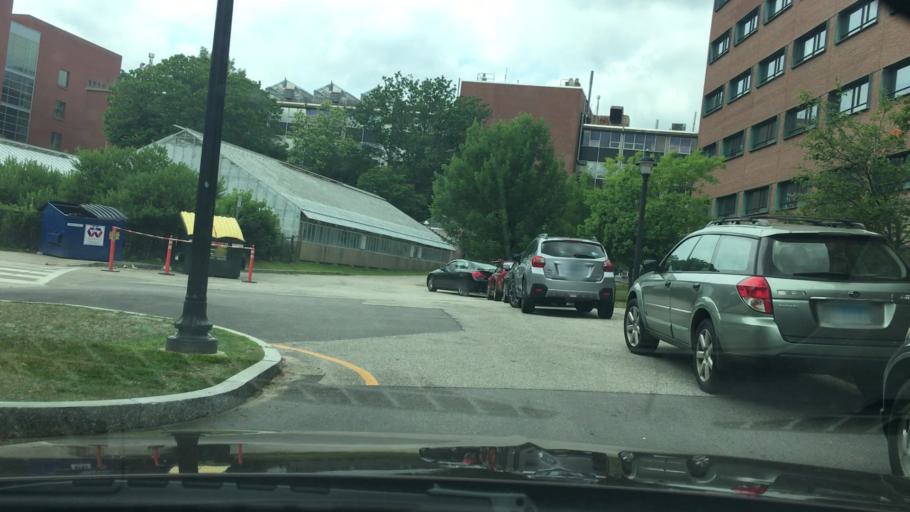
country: US
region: Connecticut
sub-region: Tolland County
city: Storrs
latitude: 41.8097
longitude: -72.2552
